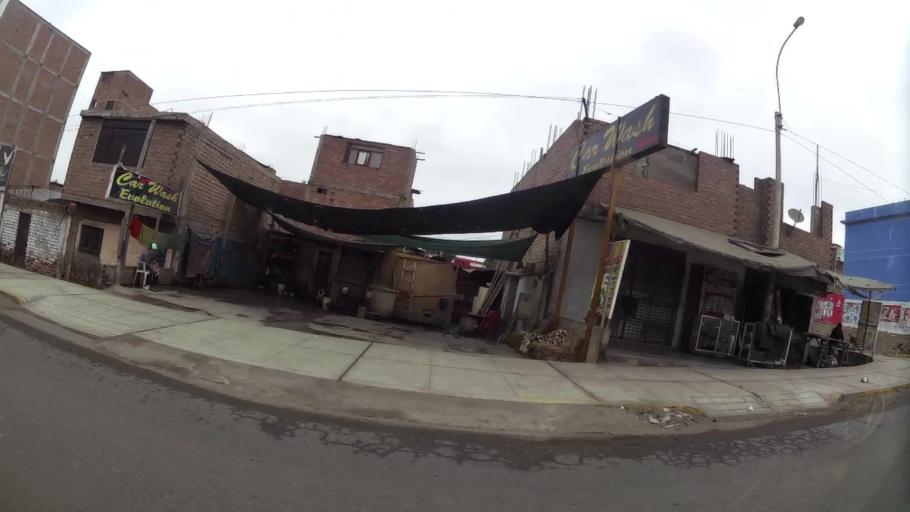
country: PE
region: Lima
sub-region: Lima
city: Surco
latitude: -12.1897
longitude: -76.9865
